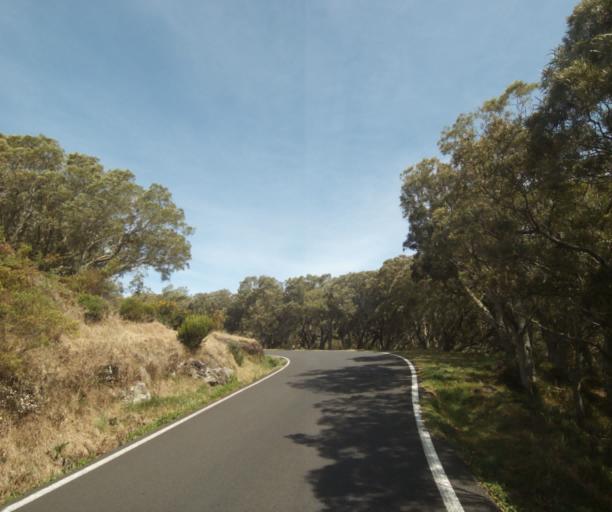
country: RE
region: Reunion
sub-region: Reunion
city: Trois-Bassins
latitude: -21.0606
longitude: 55.3771
